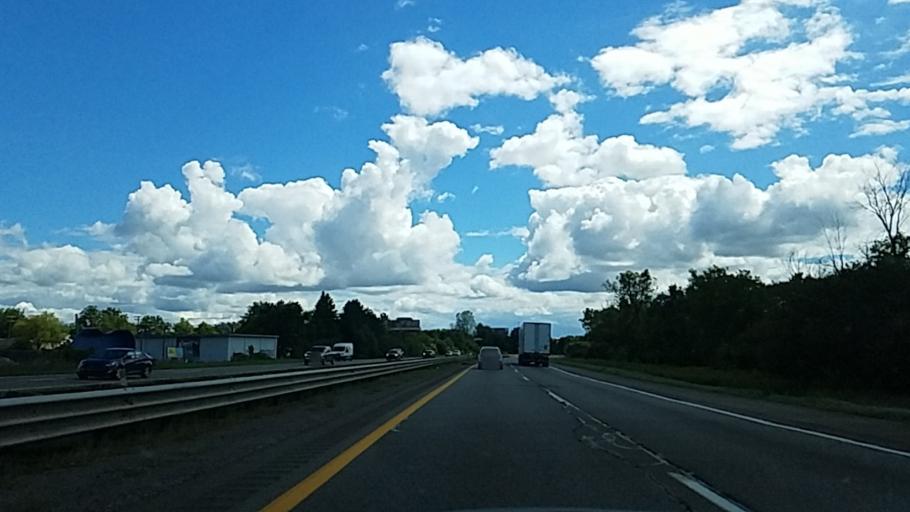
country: US
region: Michigan
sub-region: Livingston County
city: Whitmore Lake
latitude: 42.4114
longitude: -83.7639
